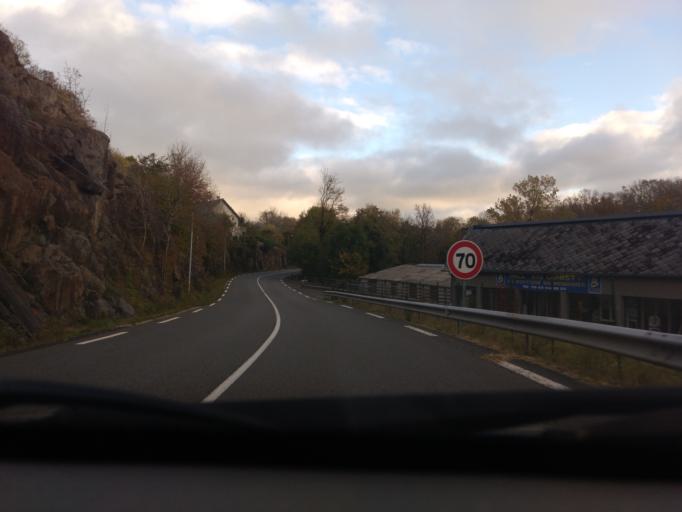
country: FR
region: Midi-Pyrenees
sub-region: Departement de l'Aveyron
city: Laguiole
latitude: 44.6790
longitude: 2.8503
